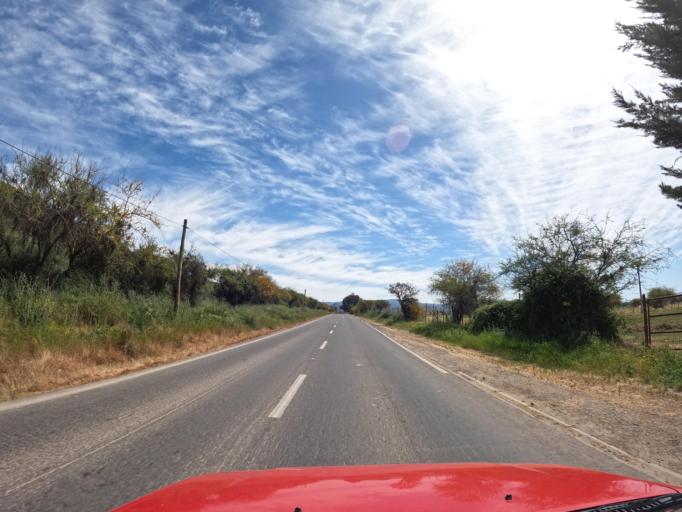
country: CL
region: Maule
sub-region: Provincia de Talca
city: Talca
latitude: -35.1214
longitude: -71.6543
